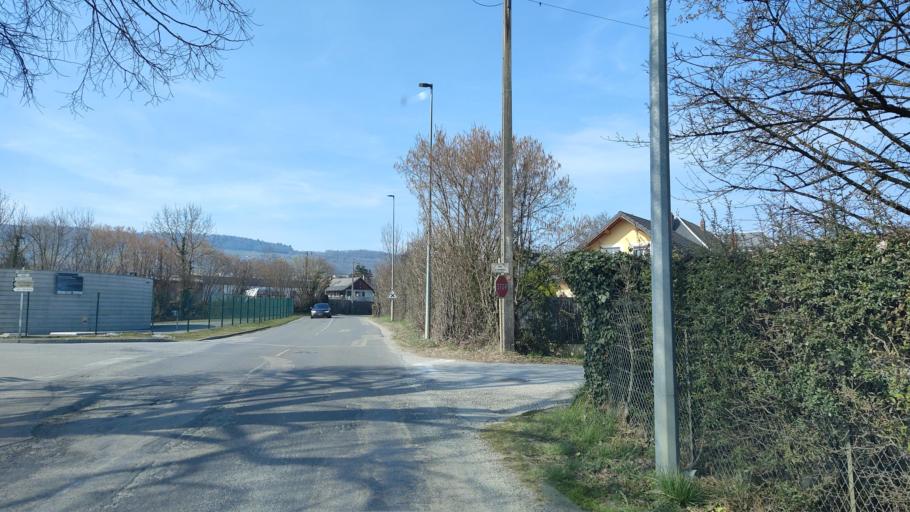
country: FR
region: Rhone-Alpes
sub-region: Departement de la Savoie
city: Albens
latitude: 45.7843
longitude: 5.9501
